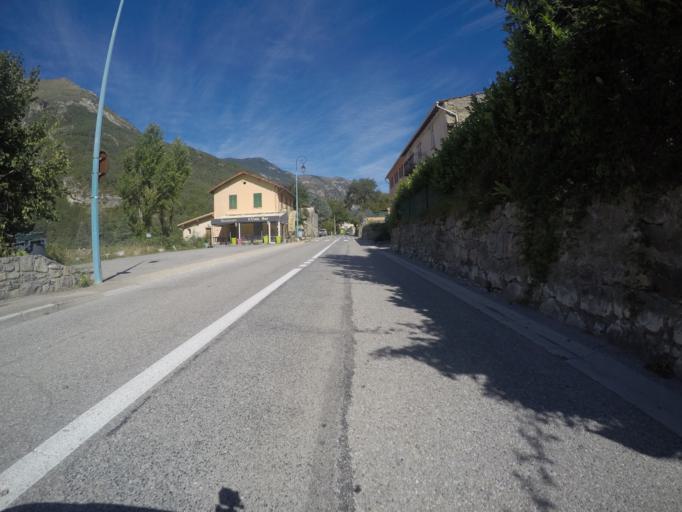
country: FR
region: Provence-Alpes-Cote d'Azur
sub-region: Departement des Alpes-Maritimes
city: Gilette
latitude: 43.9613
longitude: 7.1545
